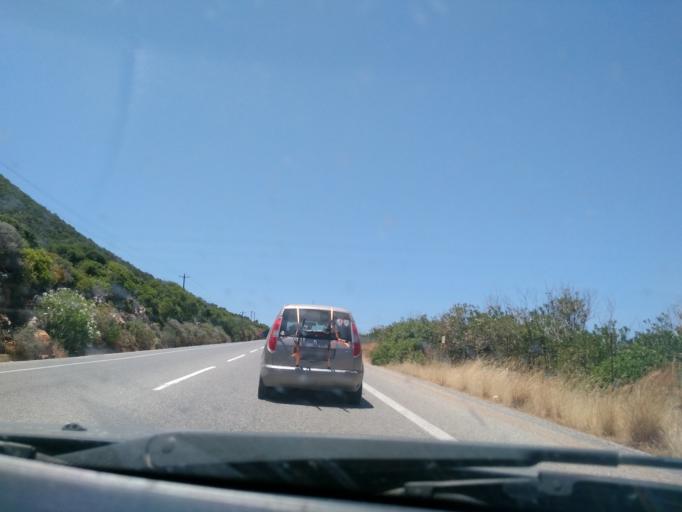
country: GR
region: Crete
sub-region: Nomos Rethymnis
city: Zoniana
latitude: 35.4061
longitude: 24.8321
